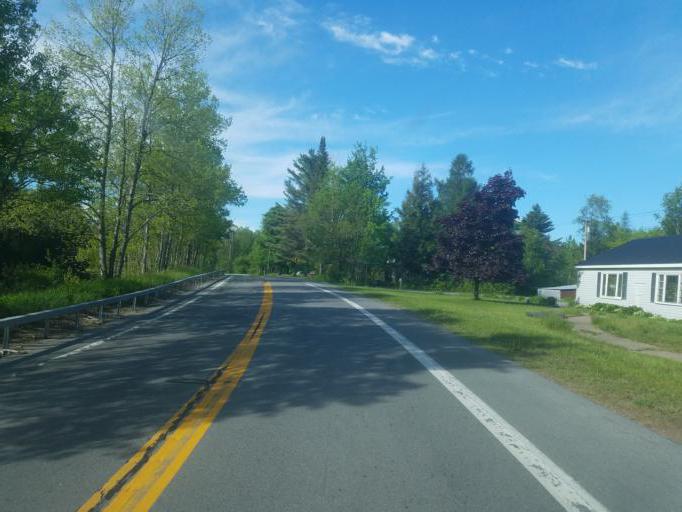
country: US
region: New York
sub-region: Herkimer County
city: Dolgeville
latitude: 43.3762
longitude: -74.9384
